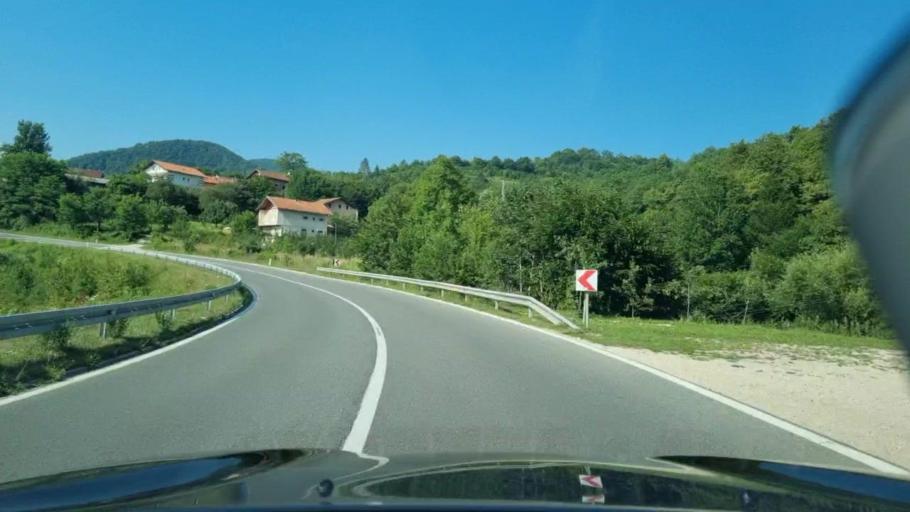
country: BA
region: Federation of Bosnia and Herzegovina
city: Jajce
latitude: 44.3531
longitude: 17.2247
